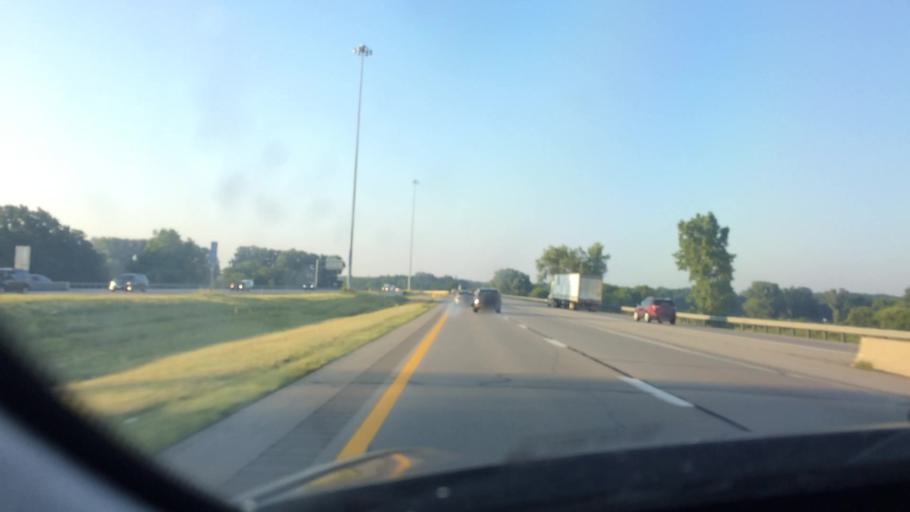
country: US
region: Ohio
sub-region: Lucas County
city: Maumee
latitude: 41.5501
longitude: -83.6848
